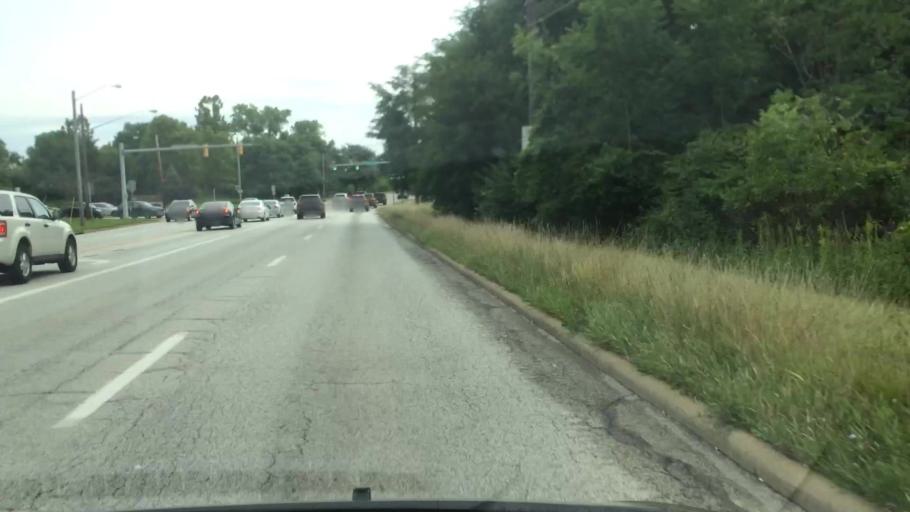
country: US
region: Ohio
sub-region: Cuyahoga County
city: Middleburg Heights
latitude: 41.3516
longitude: -81.8208
